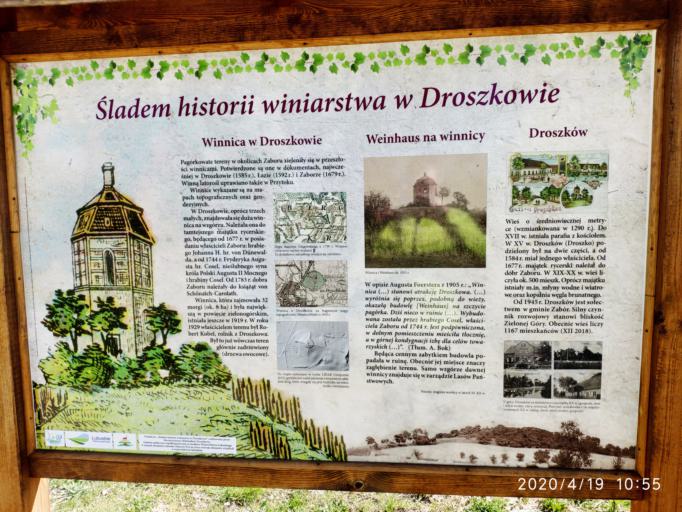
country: PL
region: Lubusz
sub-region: Powiat zielonogorski
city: Zabor
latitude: 51.9341
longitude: 15.6620
